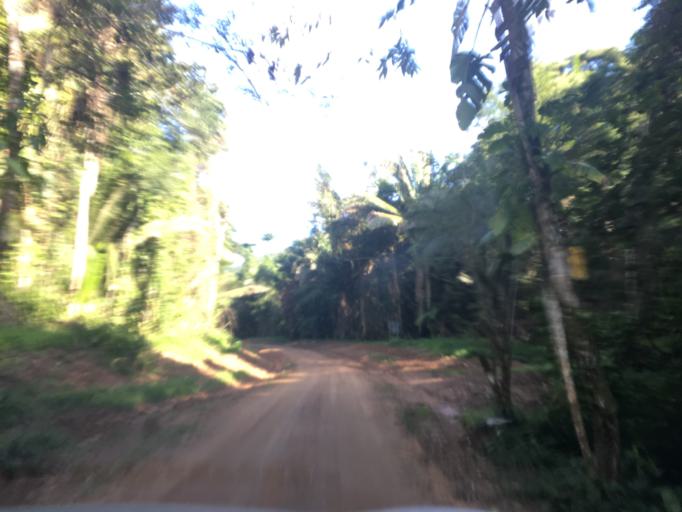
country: BZ
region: Stann Creek
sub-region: Dangriga
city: Dangriga
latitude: 16.7911
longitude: -88.4416
